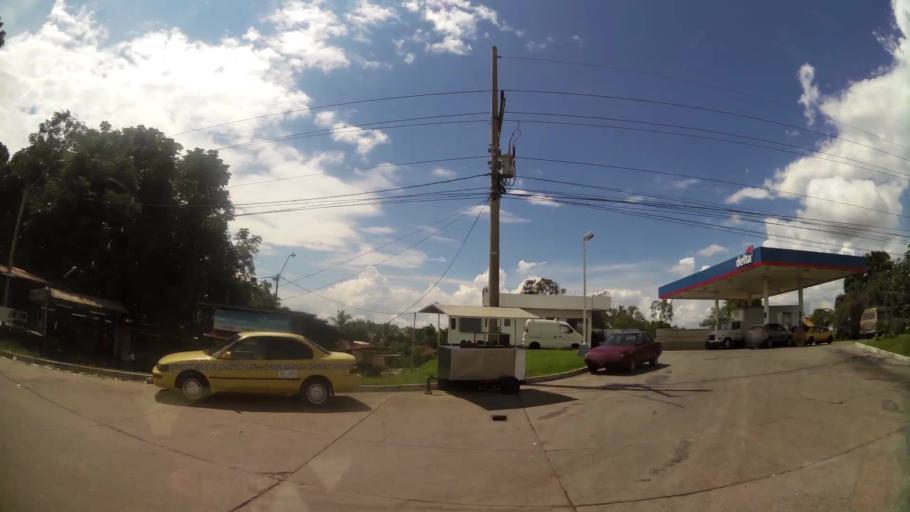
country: PA
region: Panama
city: Vista Alegre
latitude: 8.9216
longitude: -79.6971
